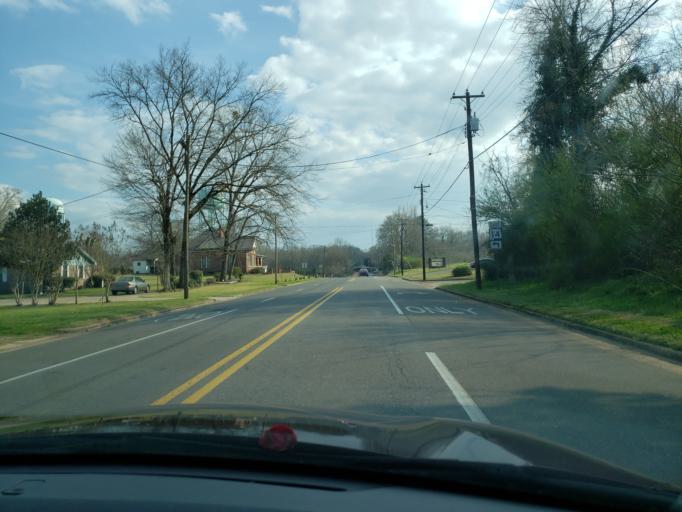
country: US
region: Alabama
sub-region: Hale County
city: Greensboro
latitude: 32.7027
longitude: -87.6069
